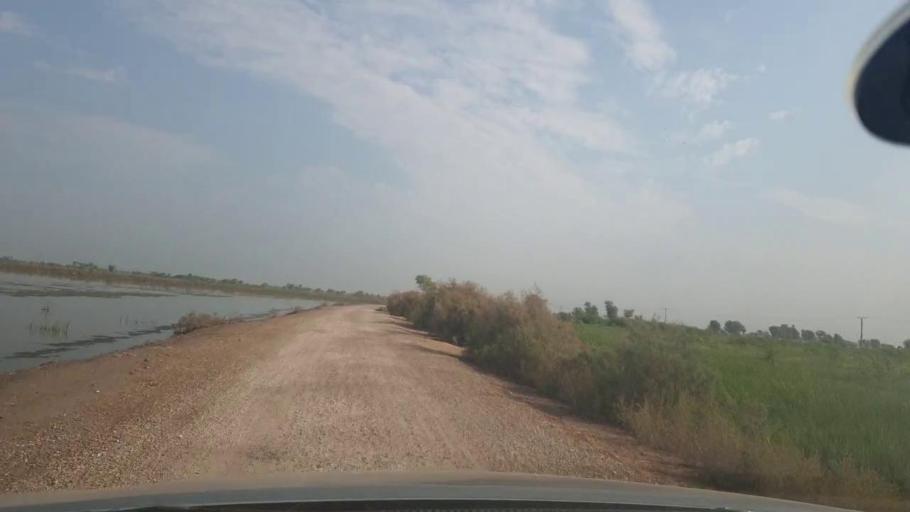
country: PK
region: Balochistan
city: Mehrabpur
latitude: 28.0650
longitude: 68.2100
